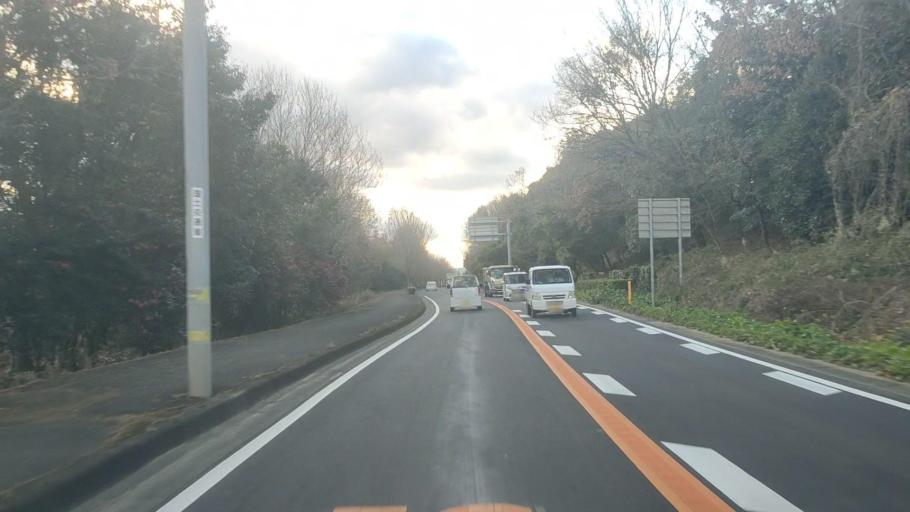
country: JP
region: Saga Prefecture
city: Saga-shi
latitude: 33.2876
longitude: 130.1612
